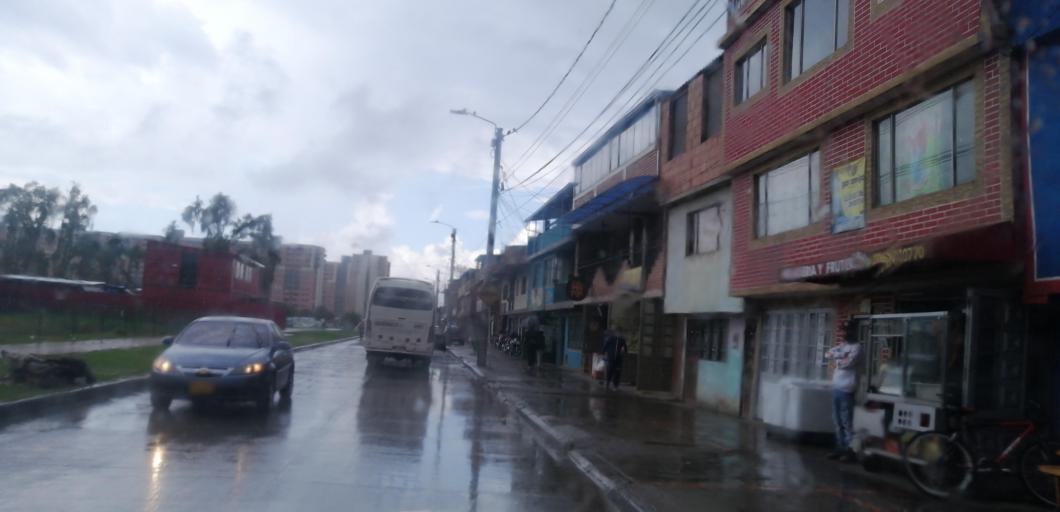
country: CO
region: Cundinamarca
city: Madrid
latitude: 4.7320
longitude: -74.2799
